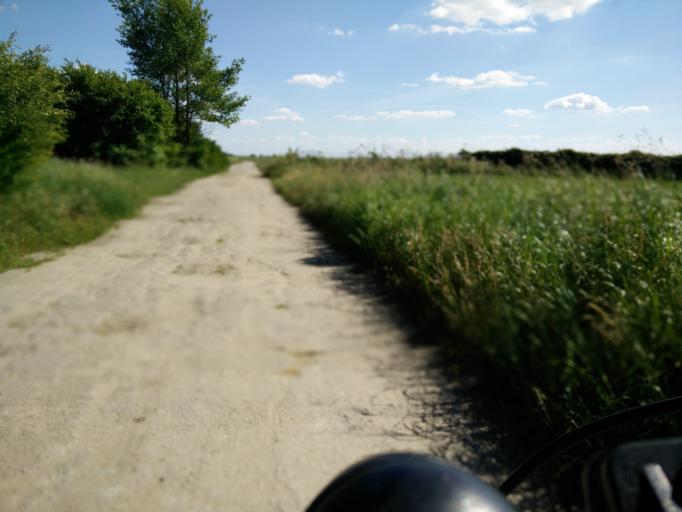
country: PL
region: Greater Poland Voivodeship
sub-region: Powiat sredzki
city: Sroda Wielkopolska
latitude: 52.2507
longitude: 17.3179
